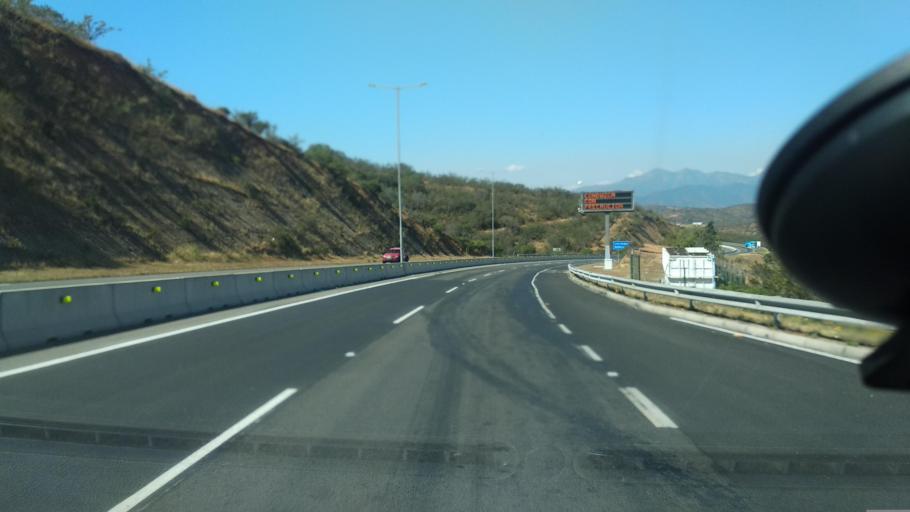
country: CL
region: Valparaiso
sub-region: Provincia de Marga Marga
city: Villa Alemana
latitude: -33.0460
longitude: -71.3247
